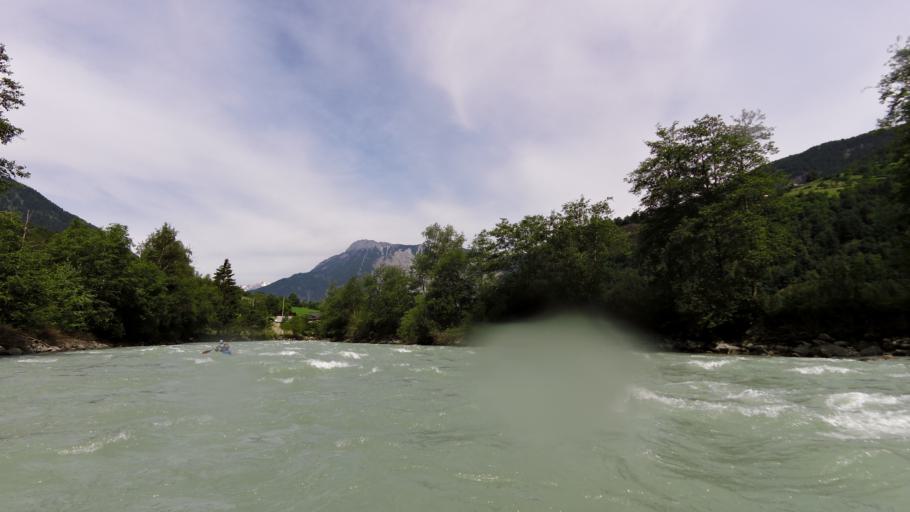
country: AT
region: Tyrol
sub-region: Politischer Bezirk Imst
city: Sautens
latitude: 47.2022
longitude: 10.8820
